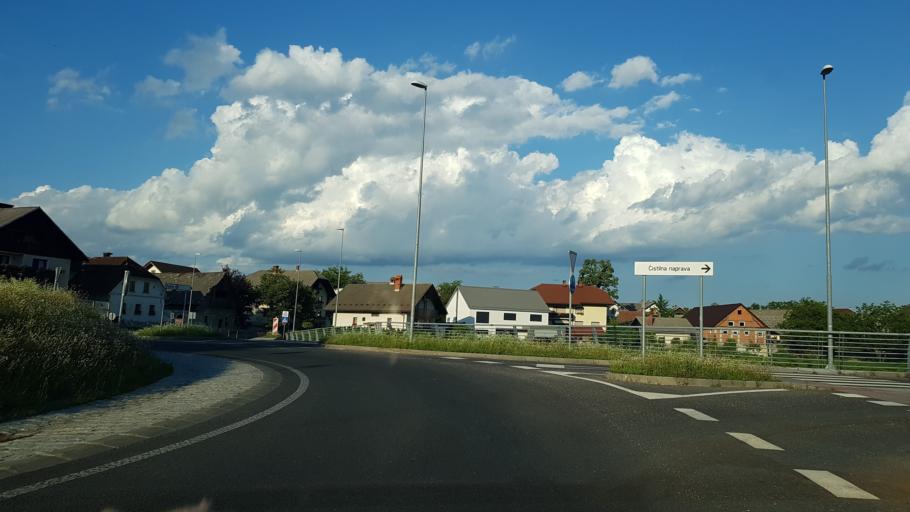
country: SI
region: Skofja Loka
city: Skofja Loka
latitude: 46.1638
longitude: 14.3216
